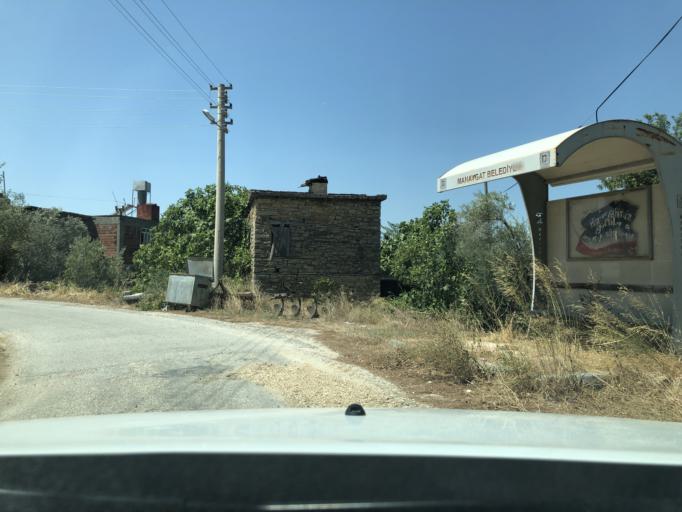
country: TR
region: Antalya
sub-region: Manavgat
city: Kizilagac
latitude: 36.8587
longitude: 31.5529
